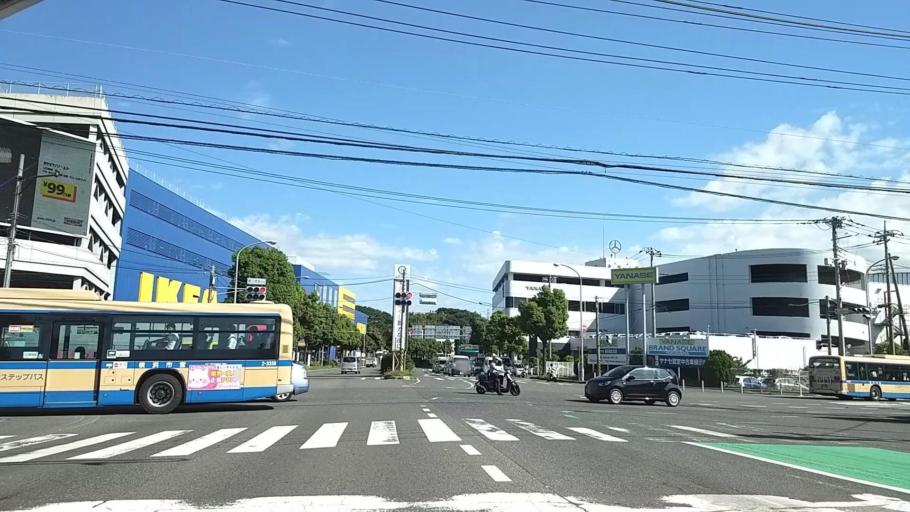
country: JP
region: Kanagawa
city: Yokohama
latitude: 35.5208
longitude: 139.5910
